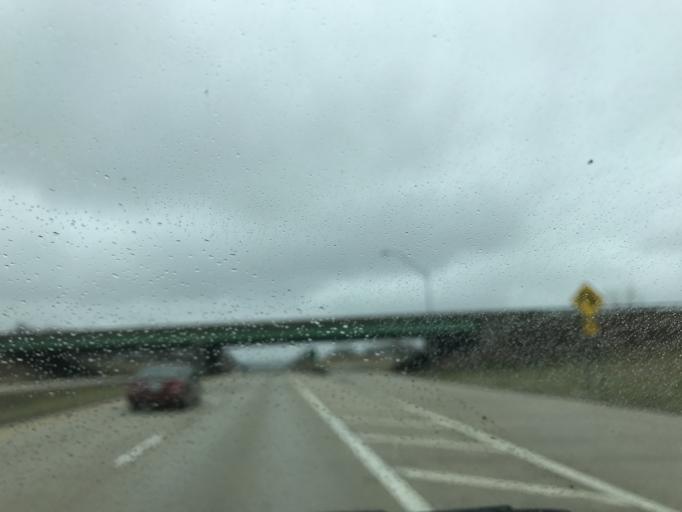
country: US
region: West Virginia
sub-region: Raleigh County
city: Daniels
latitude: 37.7732
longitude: -81.0677
